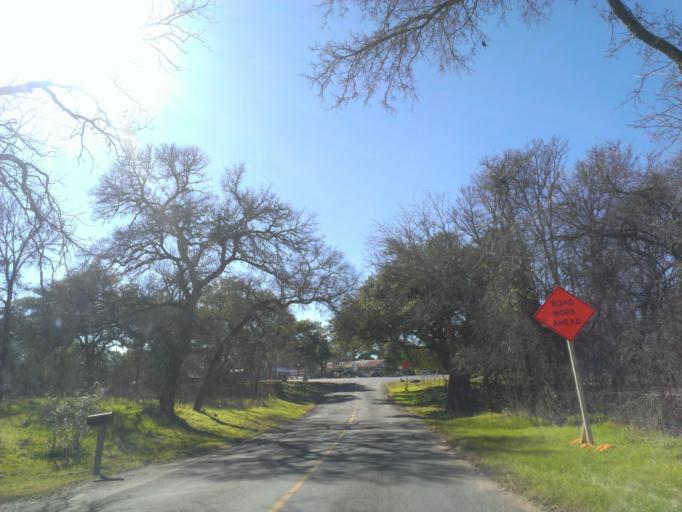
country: US
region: Texas
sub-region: Travis County
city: Briarcliff
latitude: 30.4765
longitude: -98.1557
